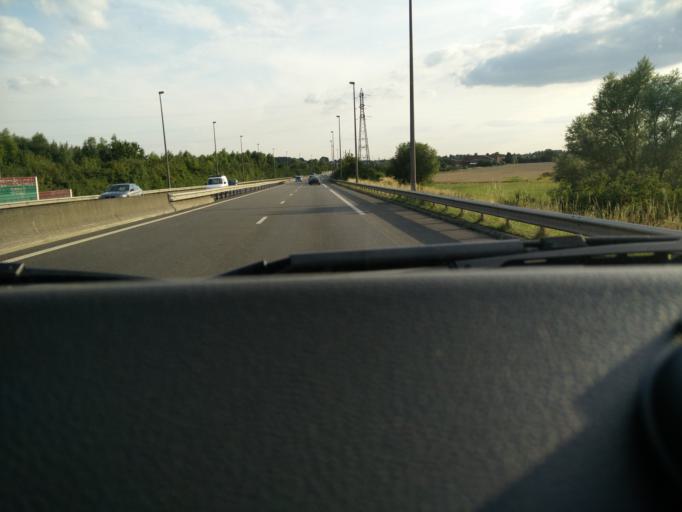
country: FR
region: Nord-Pas-de-Calais
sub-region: Departement du Nord
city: Wambrechies
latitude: 50.6745
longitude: 3.0432
